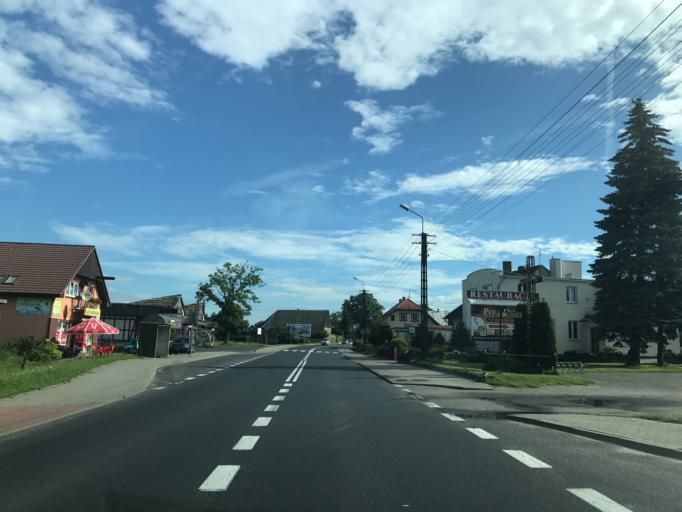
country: PL
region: West Pomeranian Voivodeship
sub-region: Powiat slawienski
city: Darlowo
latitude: 54.3096
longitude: 16.5180
